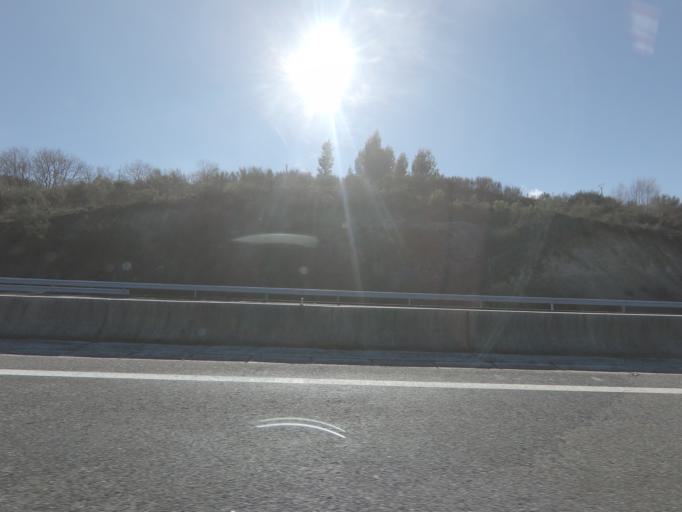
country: ES
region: Galicia
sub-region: Provincia de Pontevedra
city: Dozon
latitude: 42.5647
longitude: -8.0439
